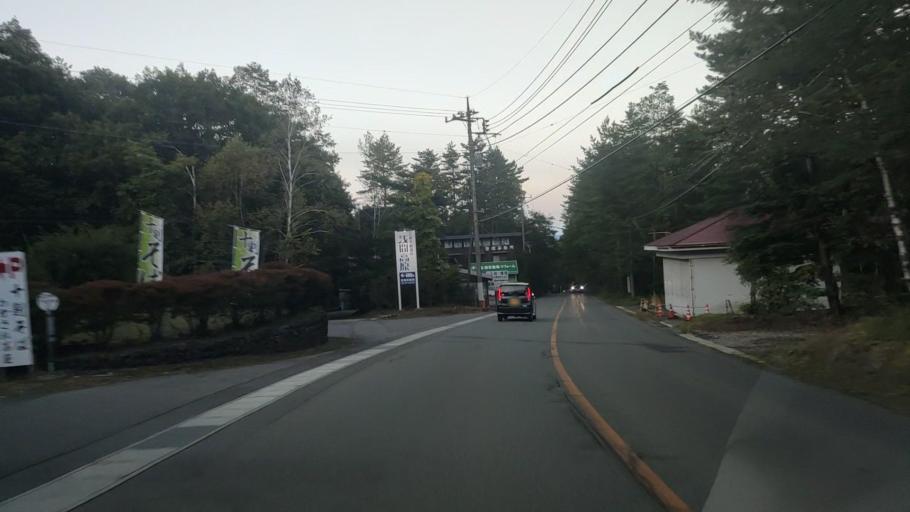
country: JP
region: Nagano
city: Komoro
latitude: 36.4393
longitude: 138.5762
